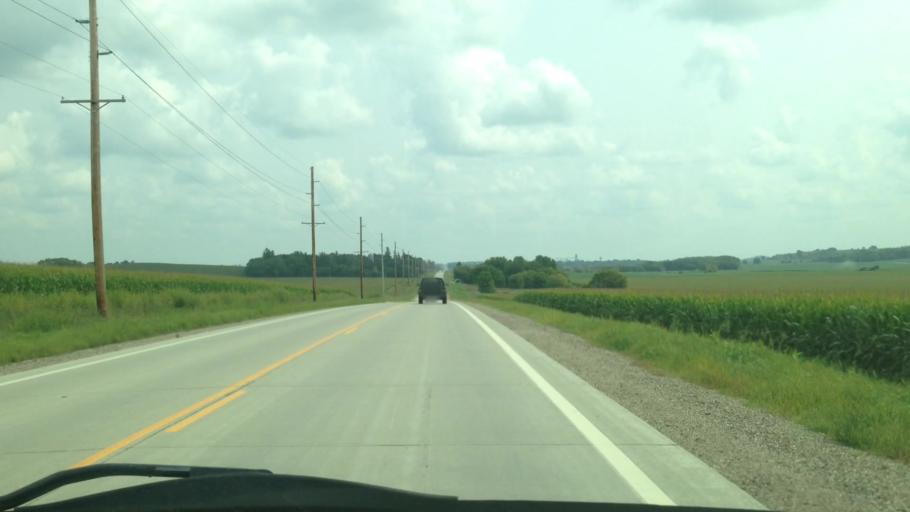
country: US
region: Minnesota
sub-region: Wabasha County
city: Elgin
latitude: 44.1367
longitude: -92.3088
